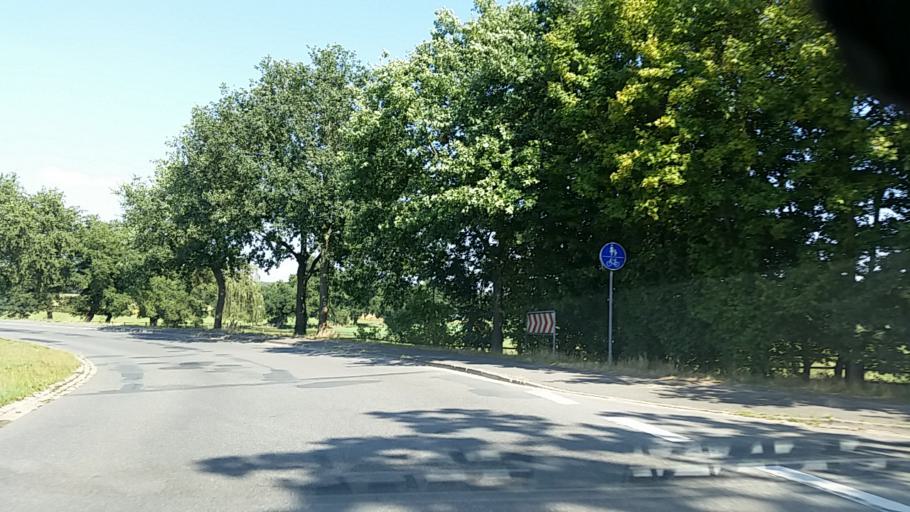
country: DE
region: Lower Saxony
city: Bad Bevensen
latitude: 53.0945
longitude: 10.5625
